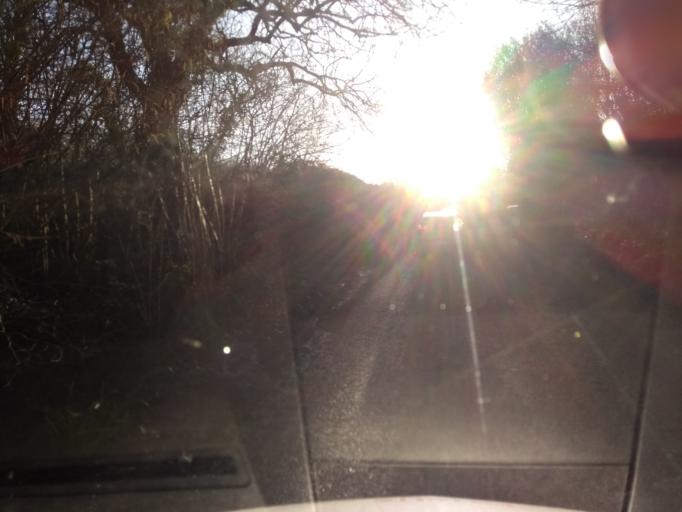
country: GB
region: England
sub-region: Somerset
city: Evercreech
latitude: 51.1333
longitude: -2.4789
